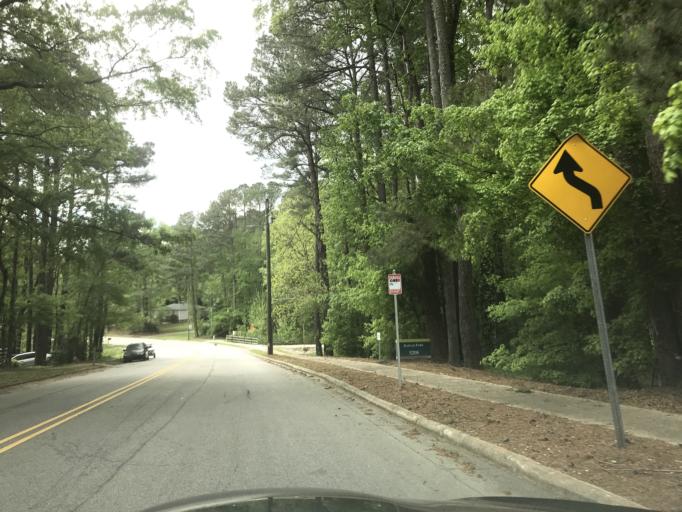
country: US
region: North Carolina
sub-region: Wake County
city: West Raleigh
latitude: 35.7751
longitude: -78.7105
